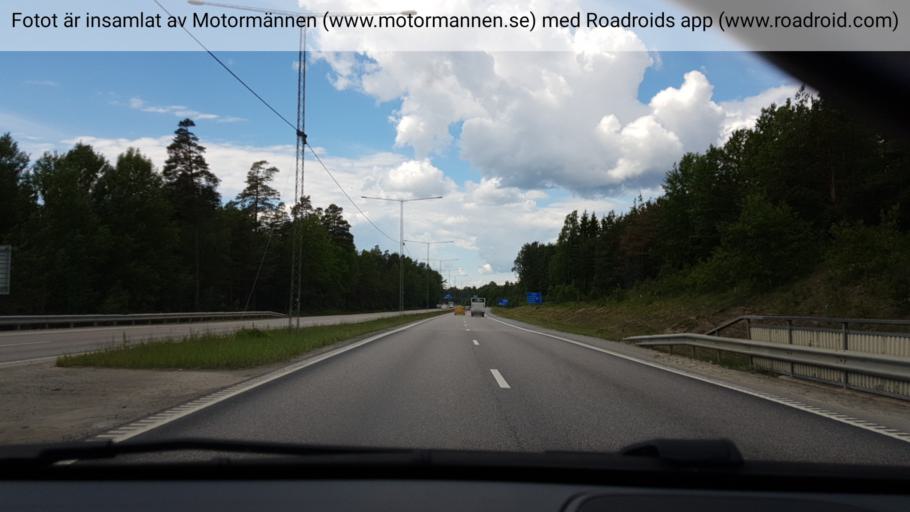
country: SE
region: Stockholm
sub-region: Haninge Kommun
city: Haninge
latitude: 59.1539
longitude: 18.1504
